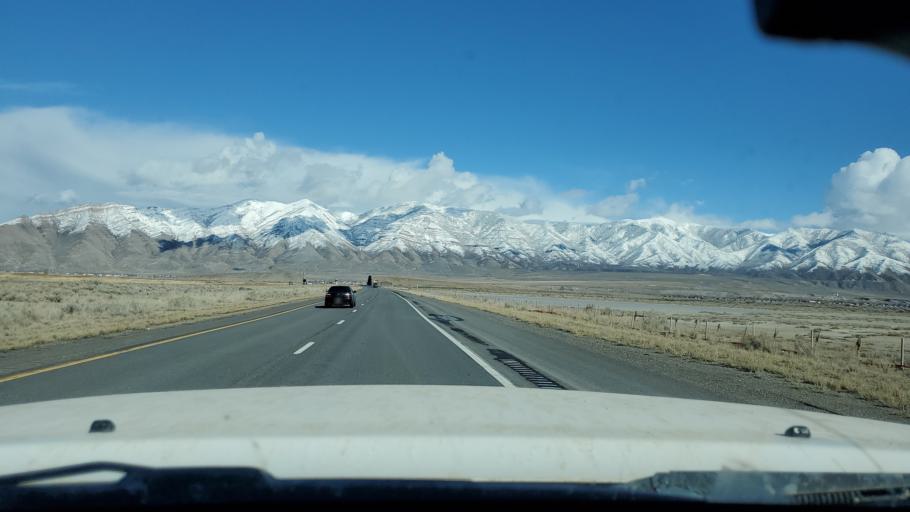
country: US
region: Utah
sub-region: Tooele County
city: Stansbury park
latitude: 40.6618
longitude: -112.3407
